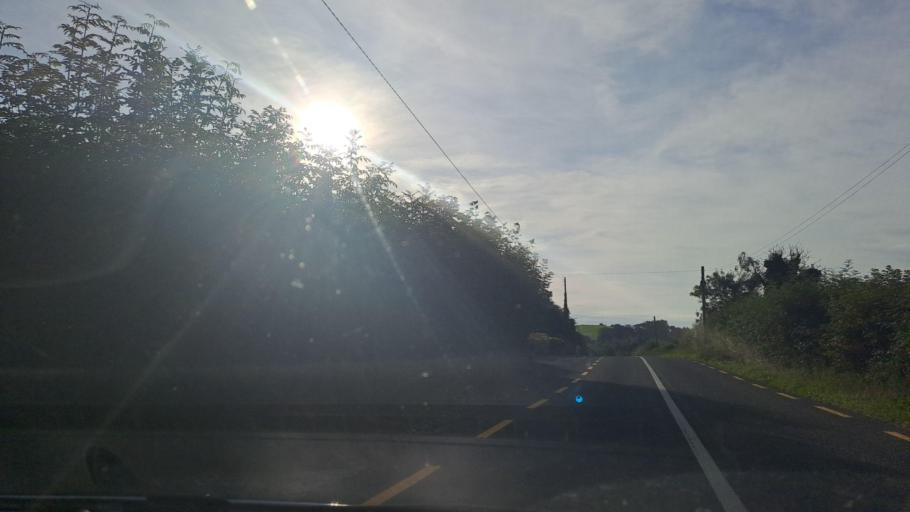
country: IE
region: Ulster
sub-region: An Cabhan
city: Kingscourt
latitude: 53.9738
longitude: -6.8726
